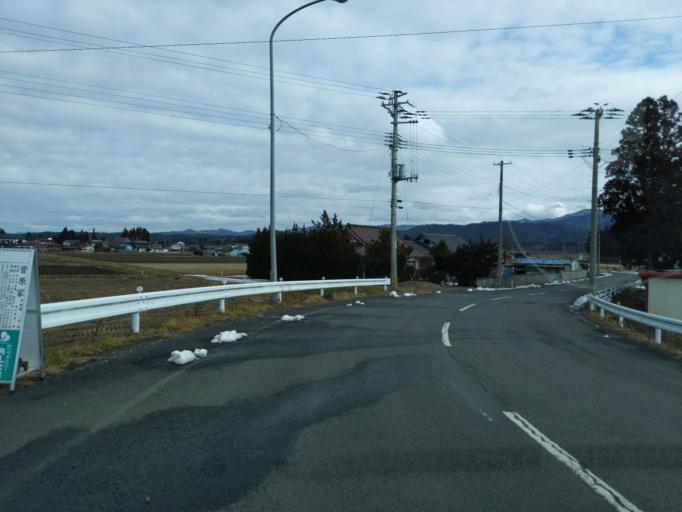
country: JP
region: Iwate
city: Mizusawa
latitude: 39.0823
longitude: 141.1671
